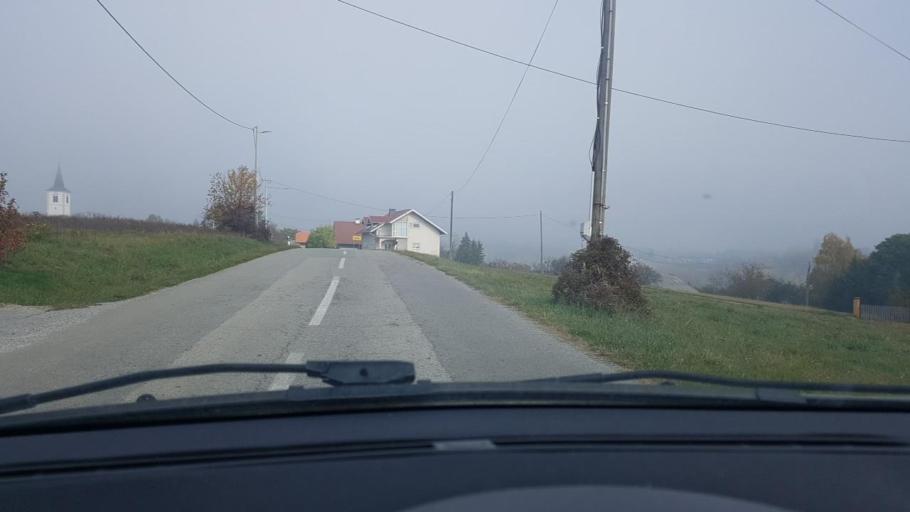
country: HR
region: Krapinsko-Zagorska
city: Zlatar
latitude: 46.1286
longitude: 16.1190
